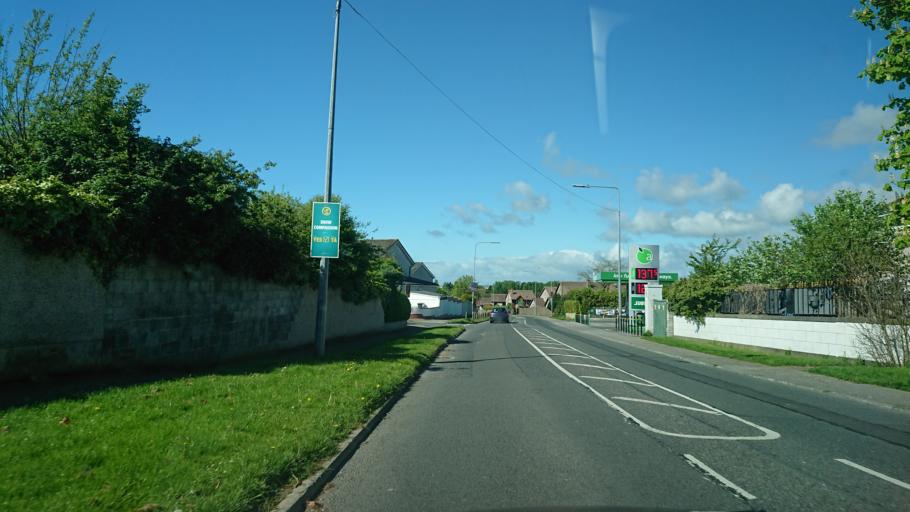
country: IE
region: Munster
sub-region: Waterford
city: Waterford
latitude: 52.2565
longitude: -7.1406
